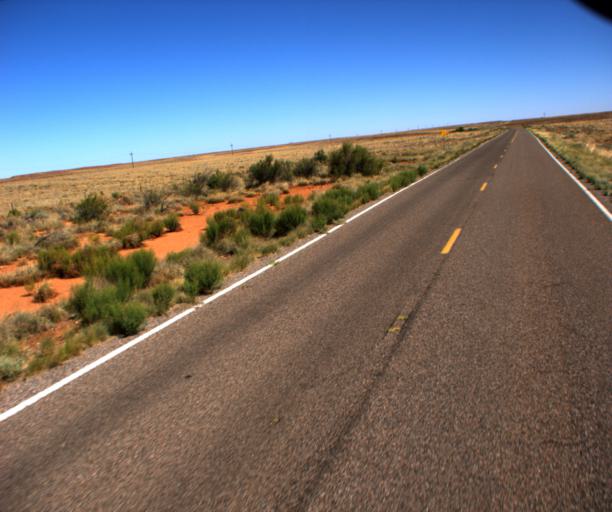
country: US
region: Arizona
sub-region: Coconino County
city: LeChee
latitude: 35.2258
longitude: -110.9548
